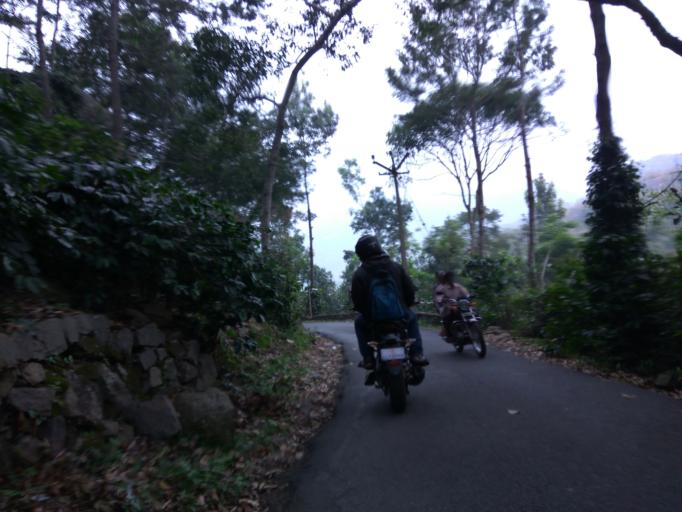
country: IN
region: Tamil Nadu
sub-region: Salem
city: Salem
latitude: 11.7890
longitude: 78.2066
